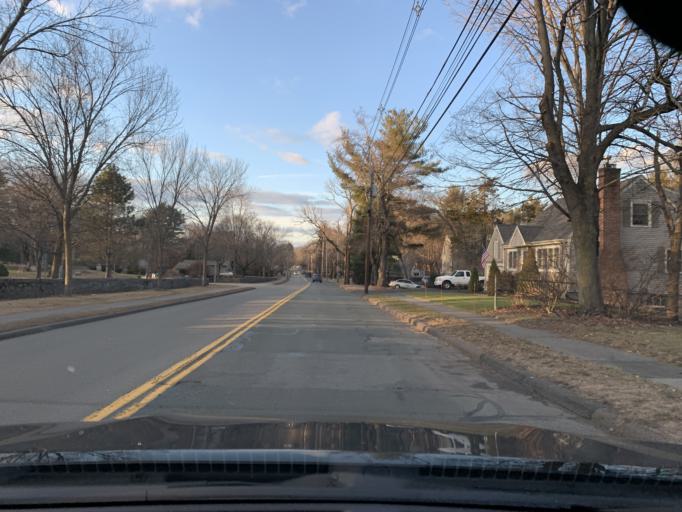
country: US
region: Massachusetts
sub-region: Essex County
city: Lynnfield
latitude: 42.5169
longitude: -71.0140
